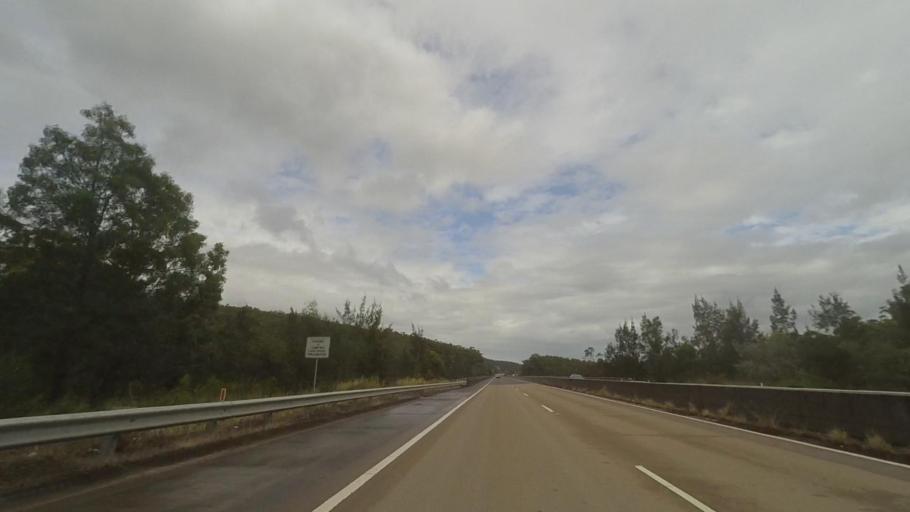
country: AU
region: New South Wales
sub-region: Port Stephens Shire
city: Medowie
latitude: -32.6231
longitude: 151.9506
